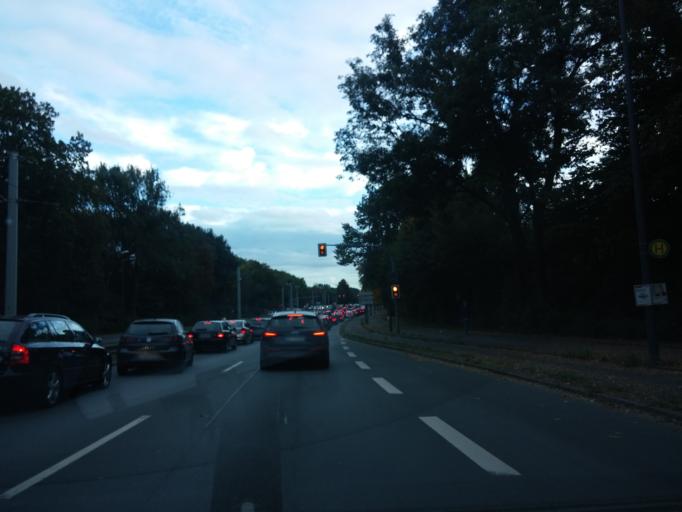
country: DE
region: North Rhine-Westphalia
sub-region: Regierungsbezirk Munster
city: Gladbeck
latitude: 51.5666
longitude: 7.0580
